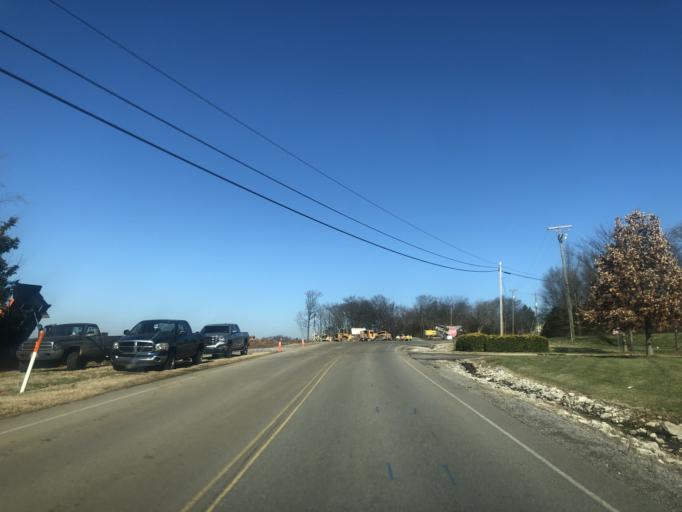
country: US
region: Tennessee
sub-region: Rutherford County
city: La Vergne
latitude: 36.0001
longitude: -86.5860
